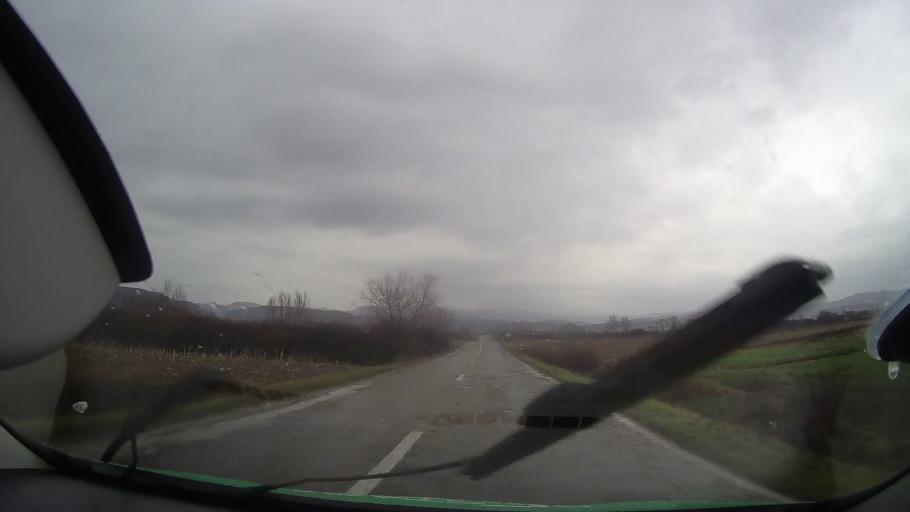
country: RO
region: Bihor
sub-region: Comuna Soimi
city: Soimi
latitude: 46.7001
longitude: 22.0903
